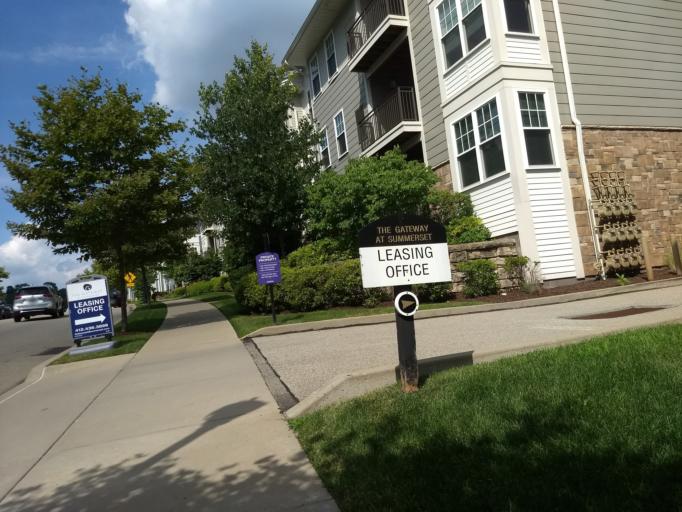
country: US
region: Pennsylvania
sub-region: Allegheny County
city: Homestead
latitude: 40.4148
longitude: -79.9217
